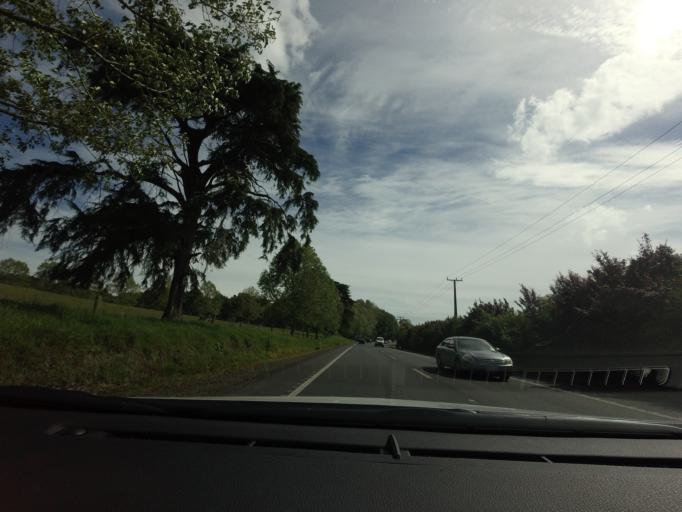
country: NZ
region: Auckland
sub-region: Auckland
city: Warkworth
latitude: -36.4202
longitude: 174.6504
